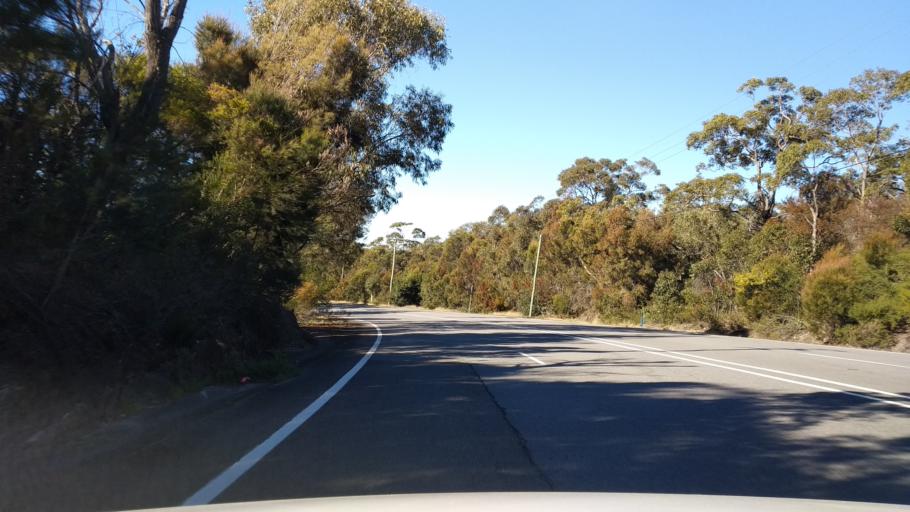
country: AU
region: New South Wales
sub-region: Gosford Shire
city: Point Clare
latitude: -33.3951
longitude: 151.2193
